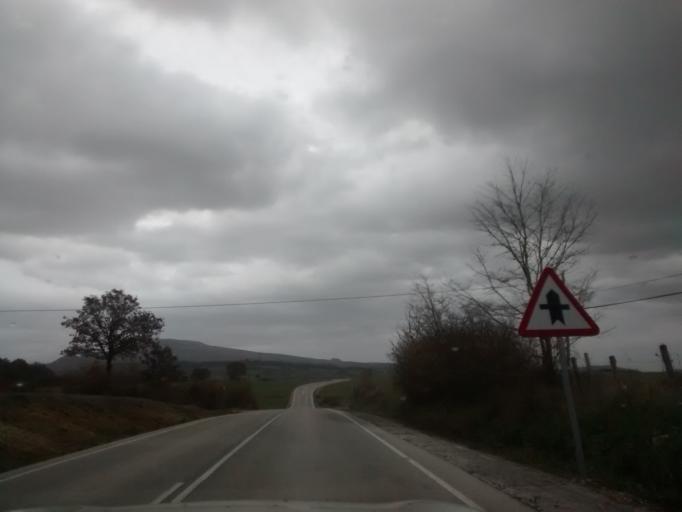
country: ES
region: Castille and Leon
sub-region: Provincia de Burgos
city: Arija
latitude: 42.9754
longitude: -3.8301
